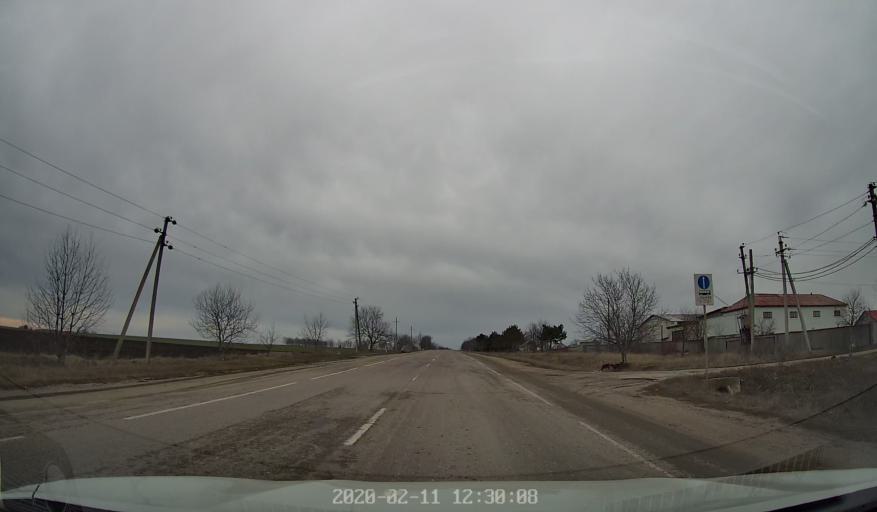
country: MD
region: Raionul Edinet
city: Edinet
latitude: 48.1600
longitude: 27.2860
